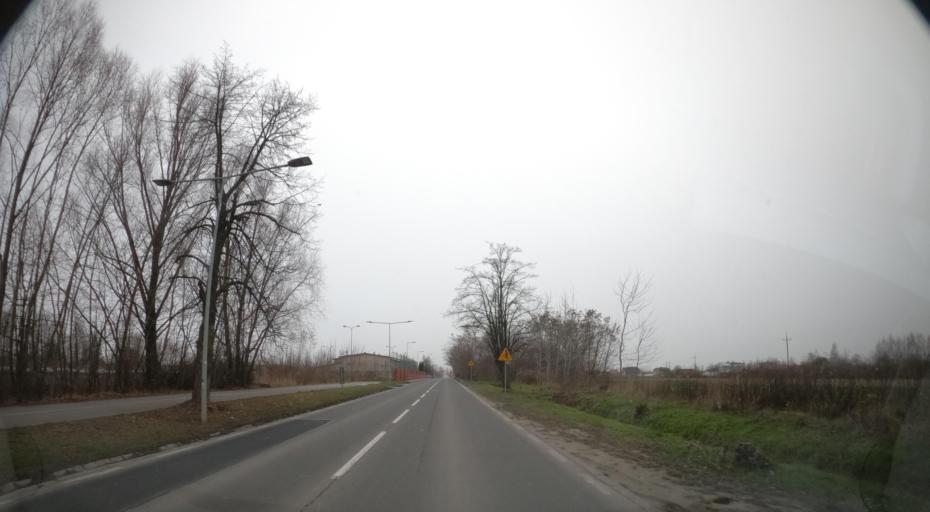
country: PL
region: Masovian Voivodeship
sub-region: Radom
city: Radom
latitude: 51.4406
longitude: 21.1892
